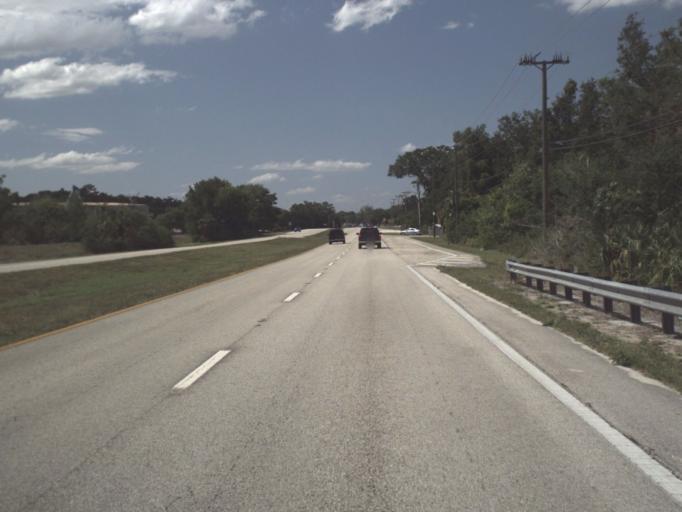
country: US
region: Florida
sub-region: Brevard County
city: Mims
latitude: 28.6543
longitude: -80.8401
